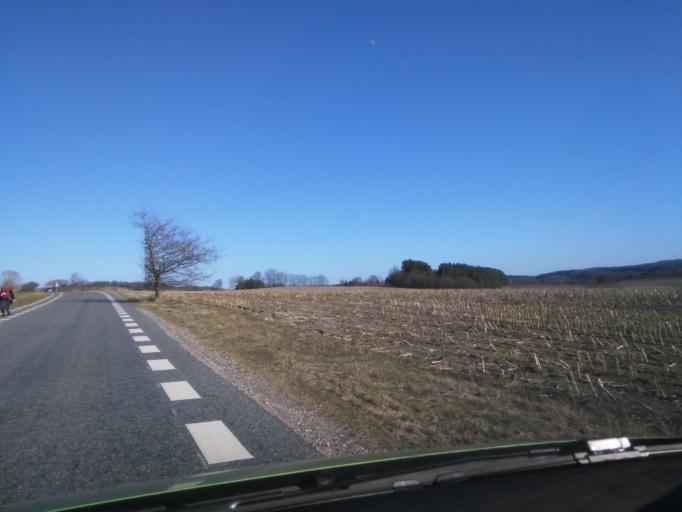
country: DK
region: Central Jutland
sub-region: Skanderborg Kommune
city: Ry
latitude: 56.1095
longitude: 9.8110
